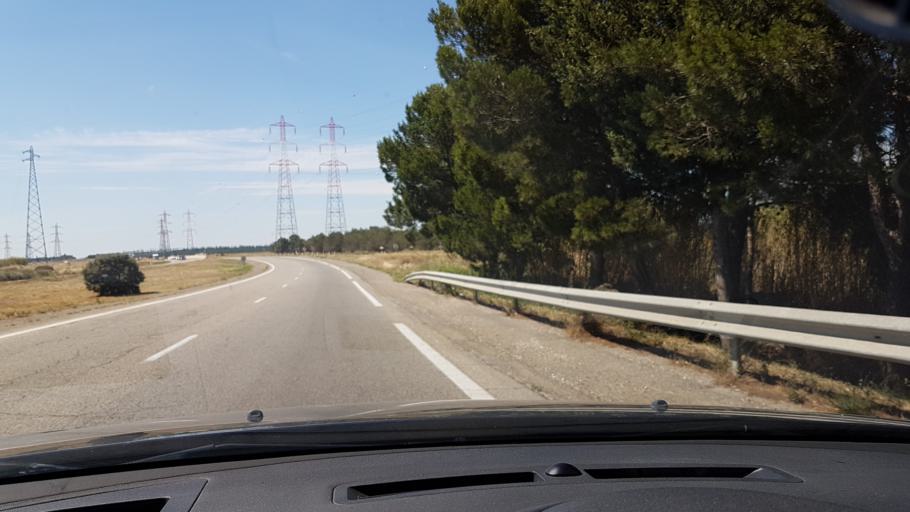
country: FR
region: Provence-Alpes-Cote d'Azur
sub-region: Departement des Bouches-du-Rhone
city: Fos-sur-Mer
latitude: 43.4800
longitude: 4.8941
